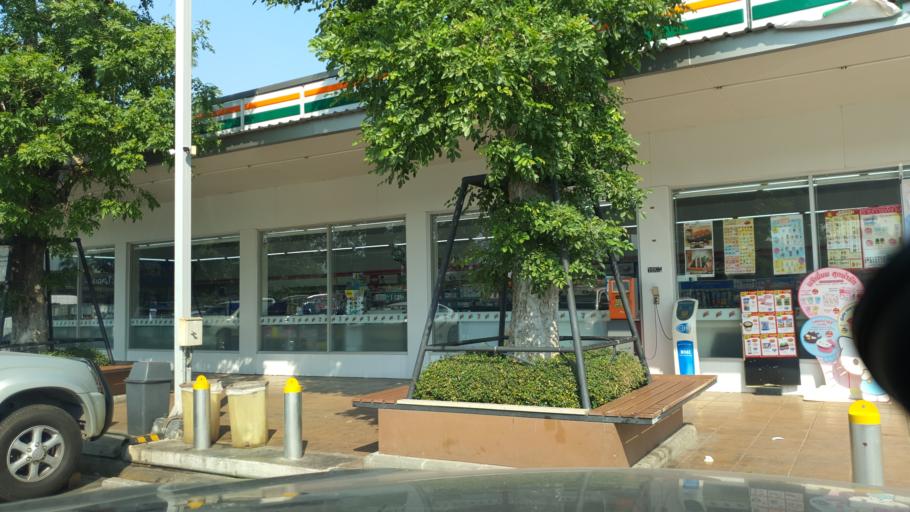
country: TH
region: Sing Buri
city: In Buri
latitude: 15.0270
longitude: 100.3368
